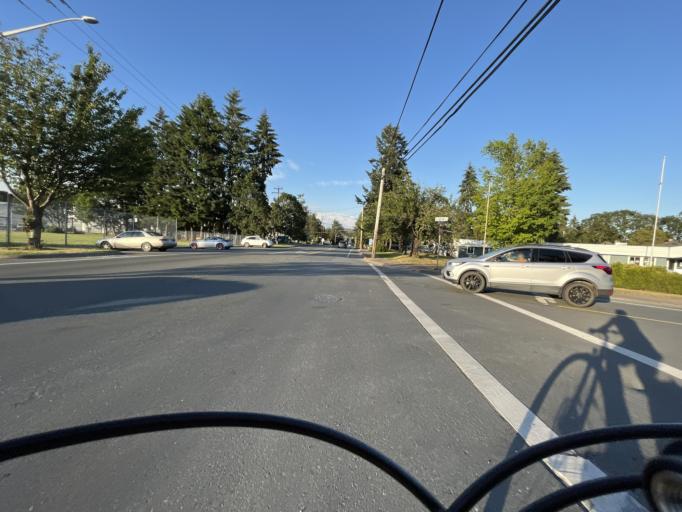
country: CA
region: British Columbia
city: Langford
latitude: 48.4497
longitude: -123.5132
